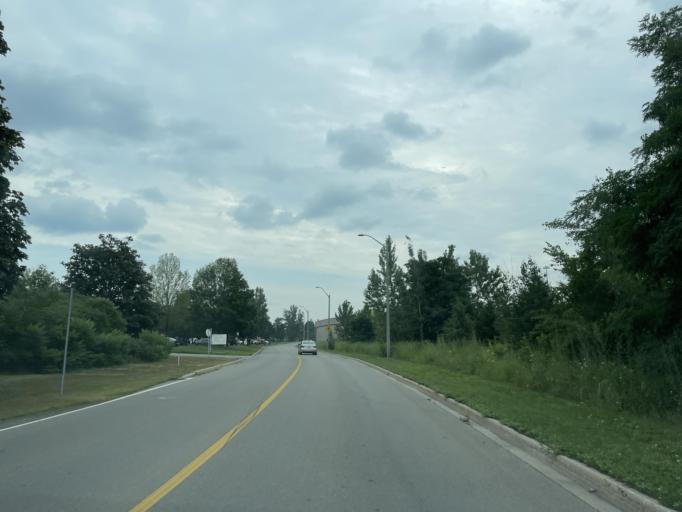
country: CA
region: Ontario
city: Hamilton
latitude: 43.2600
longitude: -79.7674
